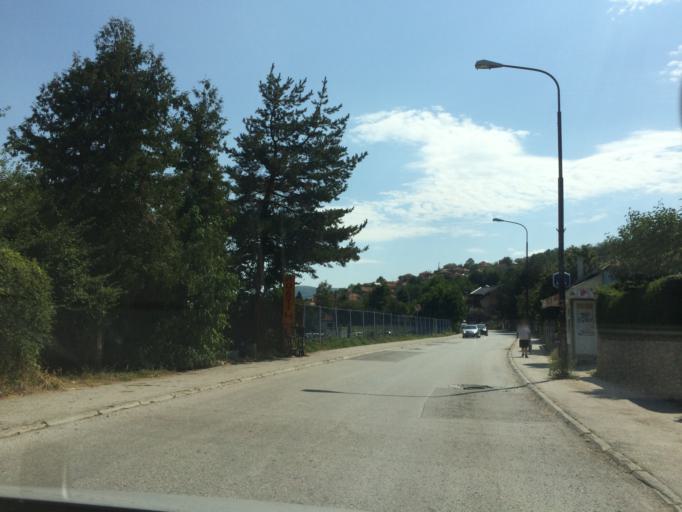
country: RS
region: Central Serbia
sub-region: Zlatiborski Okrug
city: Prijepolje
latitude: 43.3675
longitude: 19.6286
